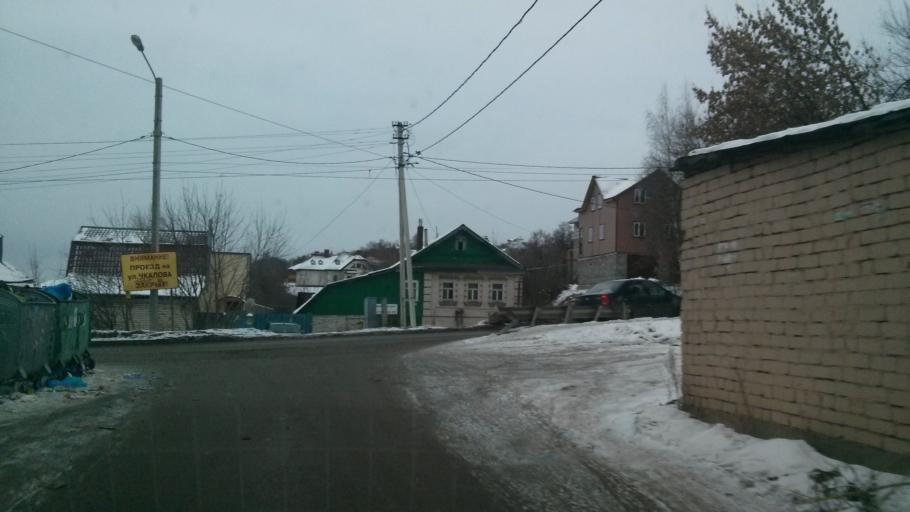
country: RU
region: Nizjnij Novgorod
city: Afonino
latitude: 56.2941
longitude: 44.0978
